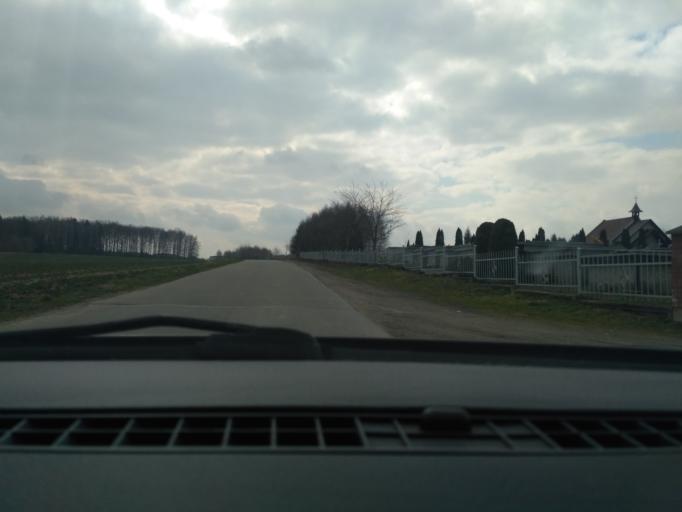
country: PL
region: Subcarpathian Voivodeship
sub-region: Powiat krosnienski
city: Kroscienko Wyzne
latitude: 49.6723
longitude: 21.8275
